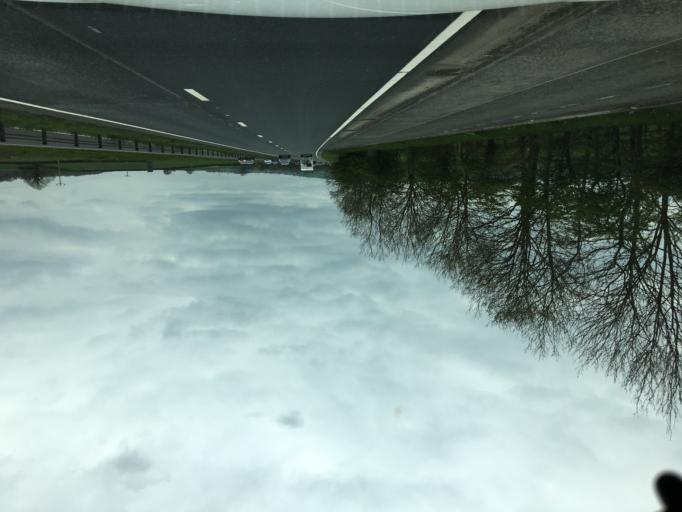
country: GB
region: Wales
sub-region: Carmarthenshire
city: Llangynog
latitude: 51.8336
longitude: -4.4315
